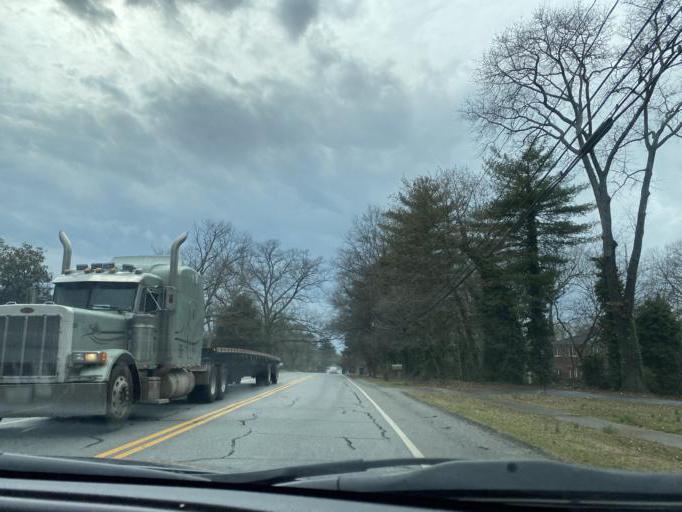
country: US
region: South Carolina
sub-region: Spartanburg County
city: Cowpens
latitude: 35.0227
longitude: -81.7966
